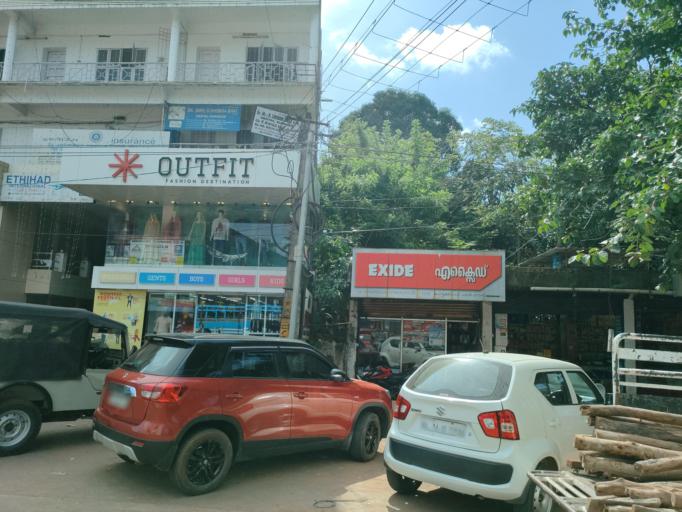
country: IN
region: Kerala
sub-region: Kasaragod District
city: Kasaragod
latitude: 12.5040
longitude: 74.9931
